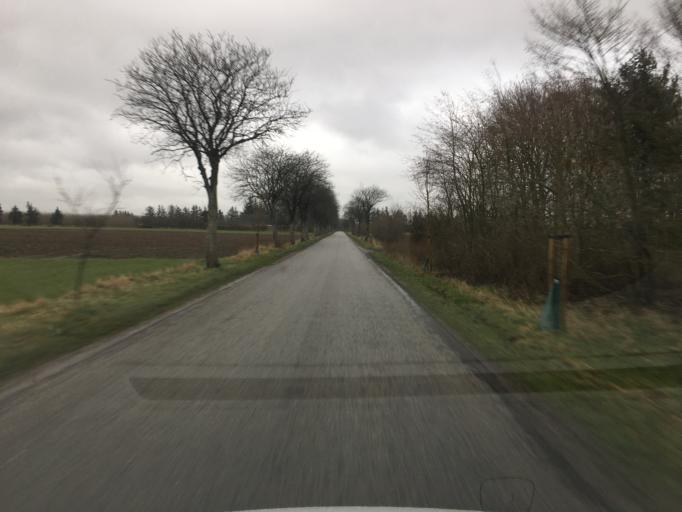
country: DK
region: South Denmark
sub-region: Aabenraa Kommune
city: Tinglev
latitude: 54.9015
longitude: 9.3162
